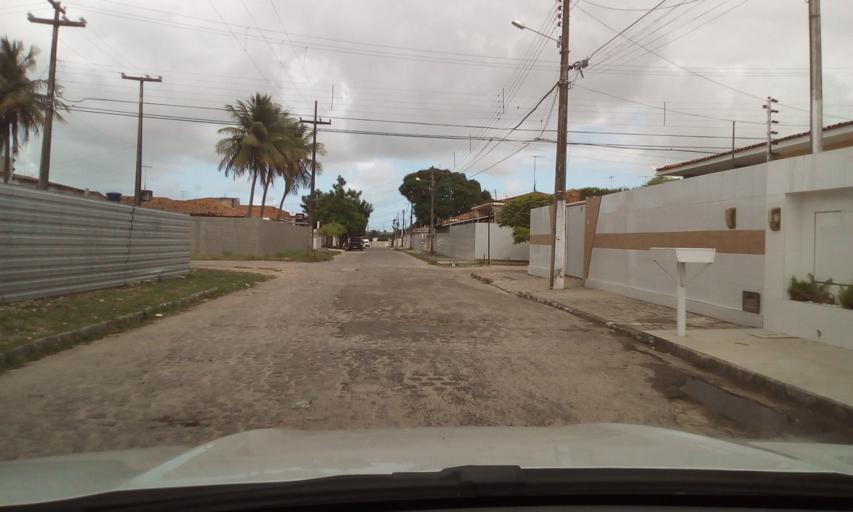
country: BR
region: Paraiba
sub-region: Joao Pessoa
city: Joao Pessoa
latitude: -7.1594
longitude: -34.8694
